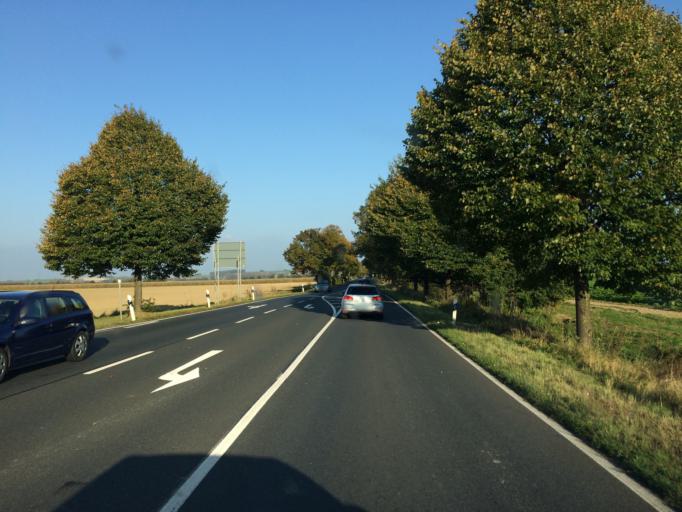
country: DE
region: Lower Saxony
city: Grossgoltern
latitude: 52.3329
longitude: 9.4678
